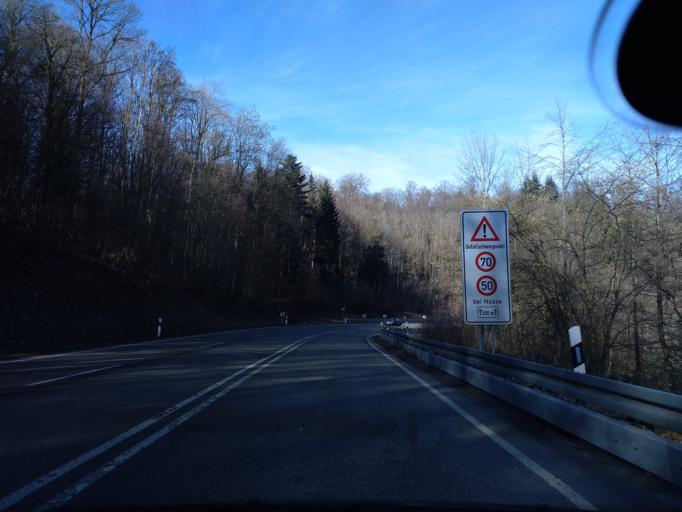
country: DE
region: Baden-Wuerttemberg
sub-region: Regierungsbezirk Stuttgart
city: Michelfeld
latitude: 49.0925
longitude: 9.6487
